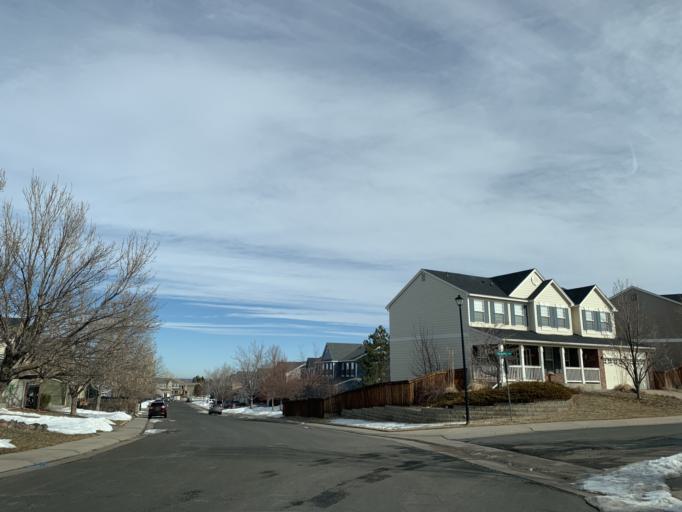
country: US
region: Colorado
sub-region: Douglas County
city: Carriage Club
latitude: 39.5333
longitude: -104.9369
